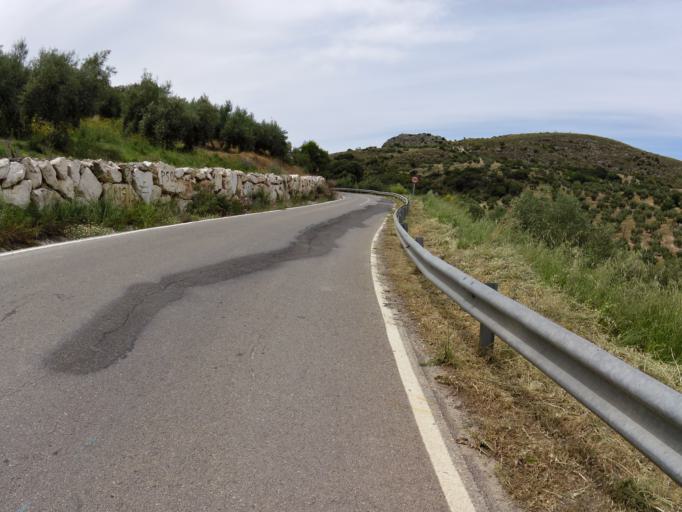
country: ES
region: Andalusia
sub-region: Province of Cordoba
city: Luque
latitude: 37.5334
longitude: -4.2566
